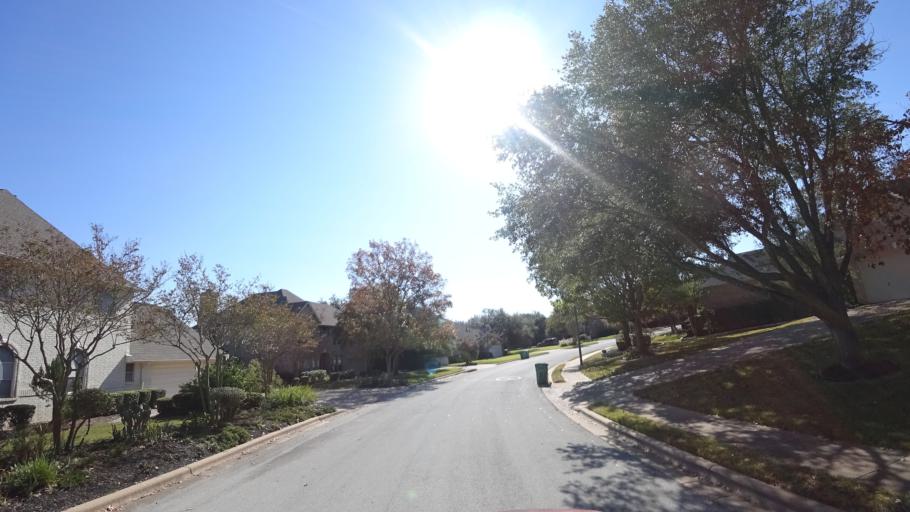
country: US
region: Texas
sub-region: Travis County
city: Lost Creek
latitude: 30.3791
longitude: -97.8514
